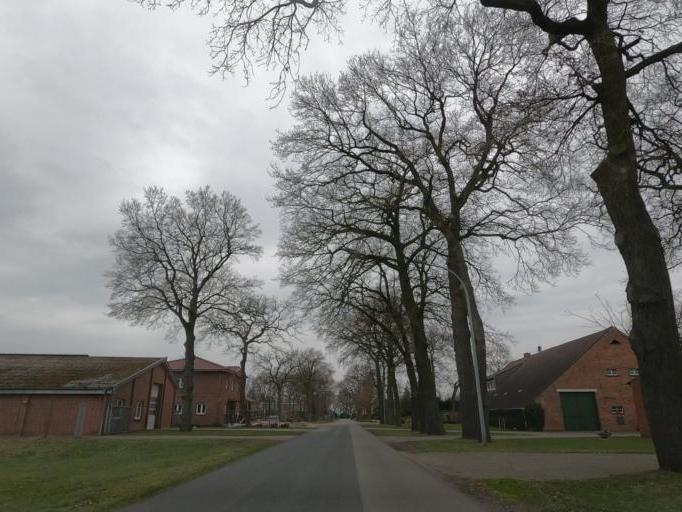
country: DE
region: Lower Saxony
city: Hilkenbrook
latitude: 52.9790
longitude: 7.7643
